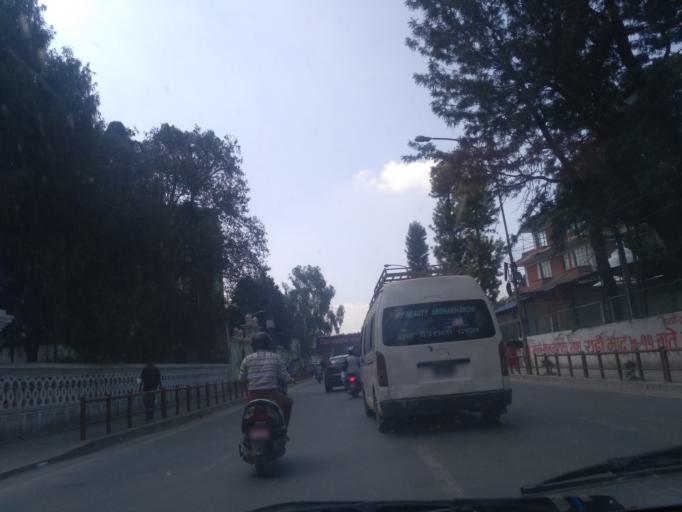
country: NP
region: Central Region
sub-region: Bagmati Zone
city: Kathmandu
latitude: 27.7074
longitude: 85.3167
